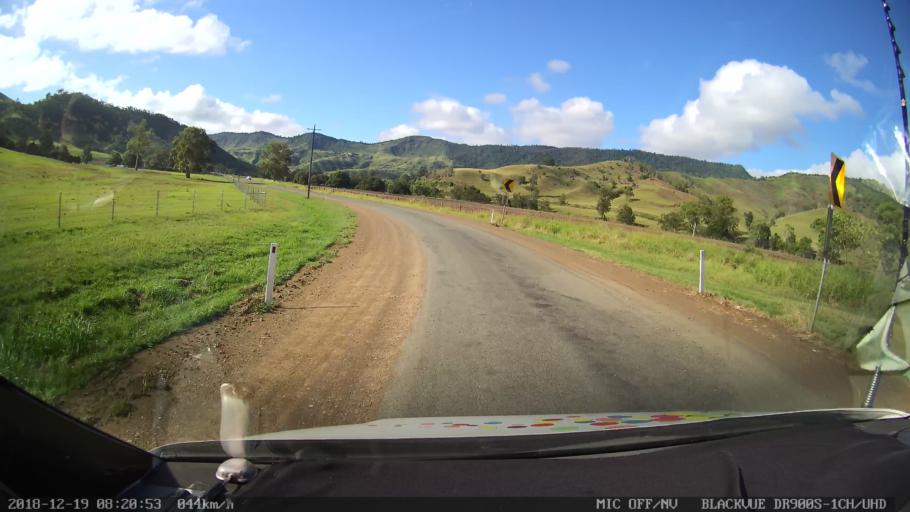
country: AU
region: New South Wales
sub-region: Kyogle
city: Kyogle
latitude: -28.2931
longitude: 152.9091
